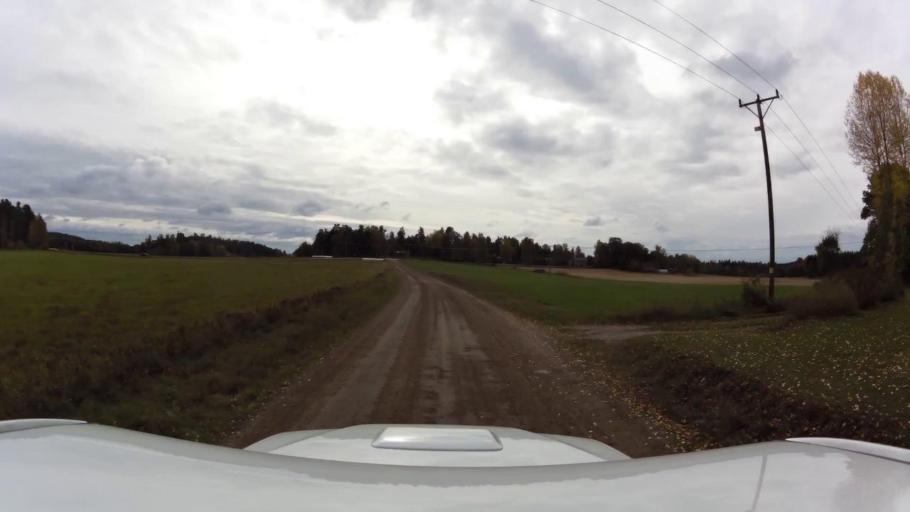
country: SE
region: OEstergoetland
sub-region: Linkopings Kommun
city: Ekangen
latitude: 58.5485
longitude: 15.6629
